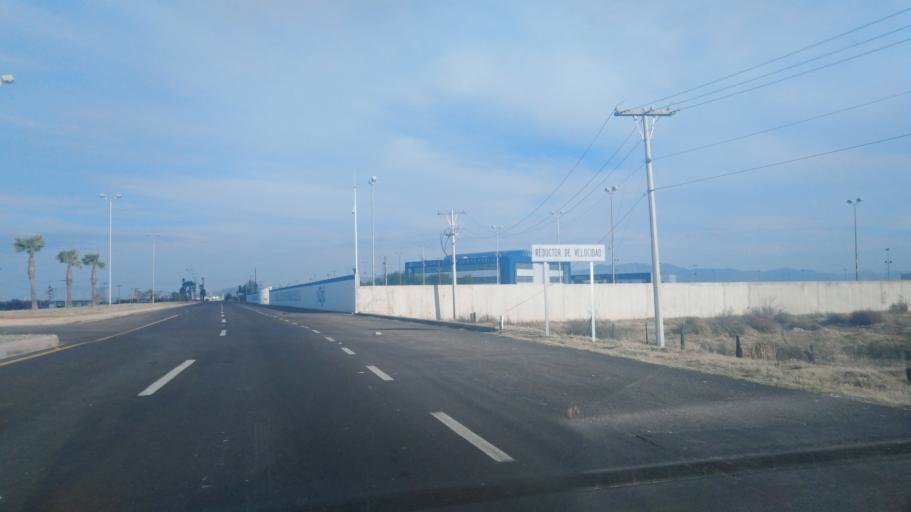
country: MX
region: Durango
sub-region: Durango
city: Jose Refugio Salcido
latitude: 24.0223
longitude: -104.5381
